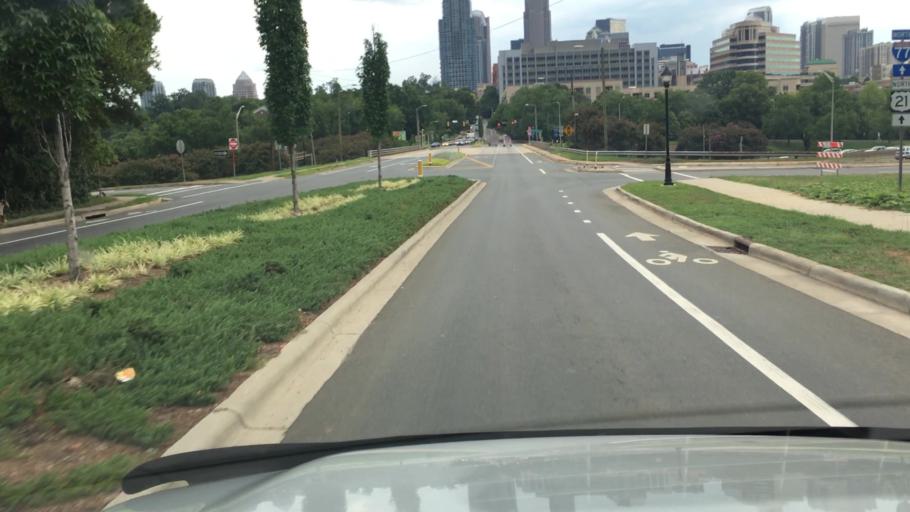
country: US
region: North Carolina
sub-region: Mecklenburg County
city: Charlotte
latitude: 35.2387
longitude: -80.8556
